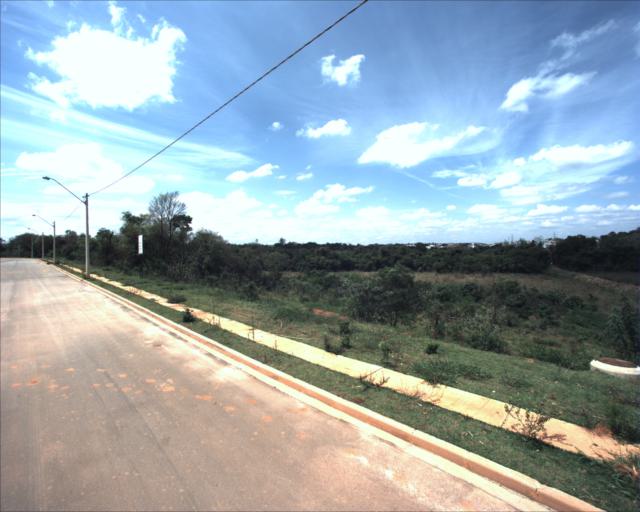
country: BR
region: Sao Paulo
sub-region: Sorocaba
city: Sorocaba
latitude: -23.4093
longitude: -47.4053
